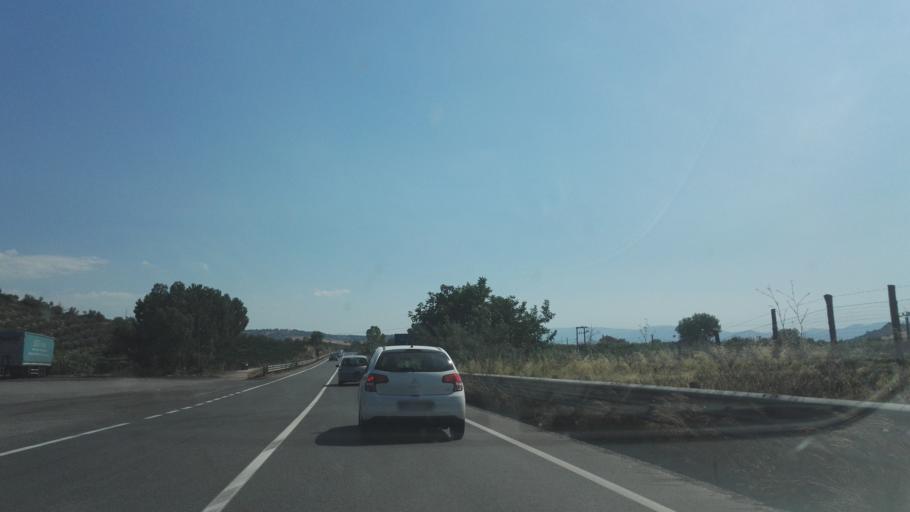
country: IT
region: Calabria
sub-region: Provincia di Cosenza
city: San Lorenzo del Vallo
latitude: 39.6712
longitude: 16.2700
